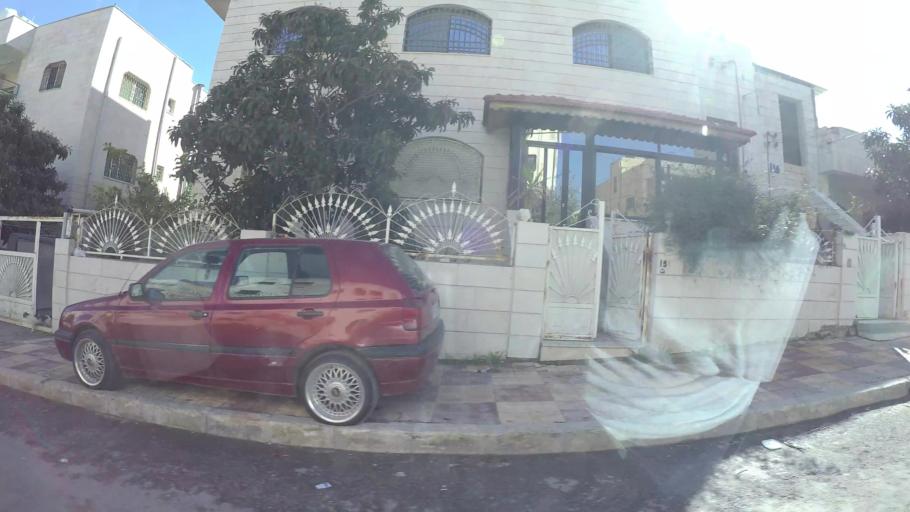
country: JO
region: Amman
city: Al Bunayyat ash Shamaliyah
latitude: 31.9061
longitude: 35.9013
